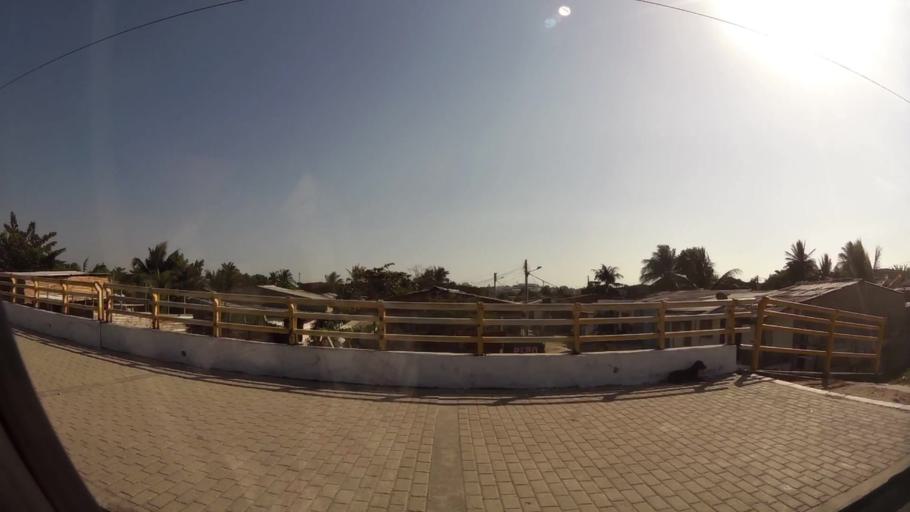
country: CO
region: Bolivar
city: Cartagena
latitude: 10.4149
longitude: -75.5025
